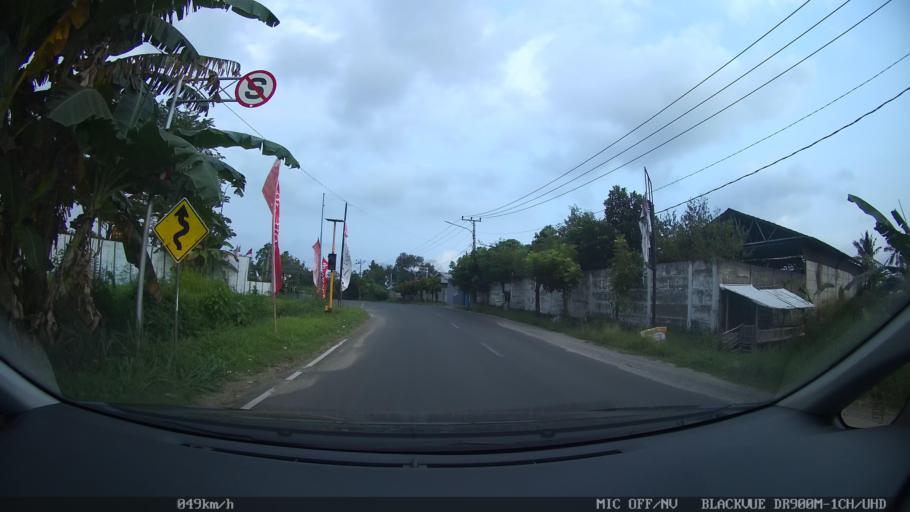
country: ID
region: Lampung
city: Bandarlampung
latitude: -5.4297
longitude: 105.2371
